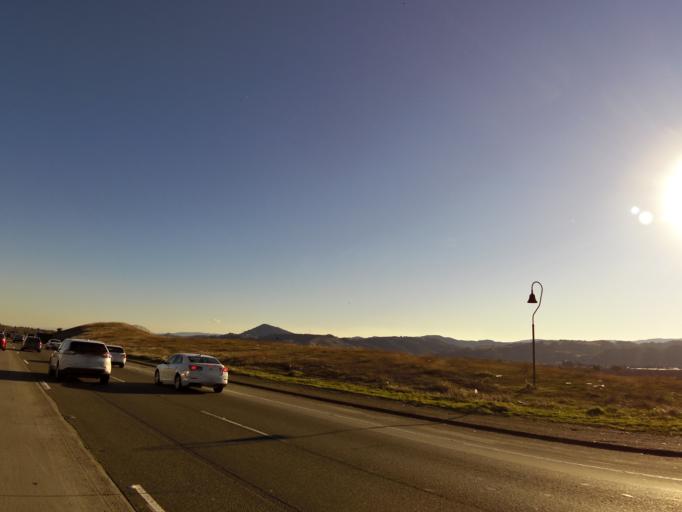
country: US
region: California
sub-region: Santa Clara County
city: Morgan Hill
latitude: 37.1821
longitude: -121.6831
